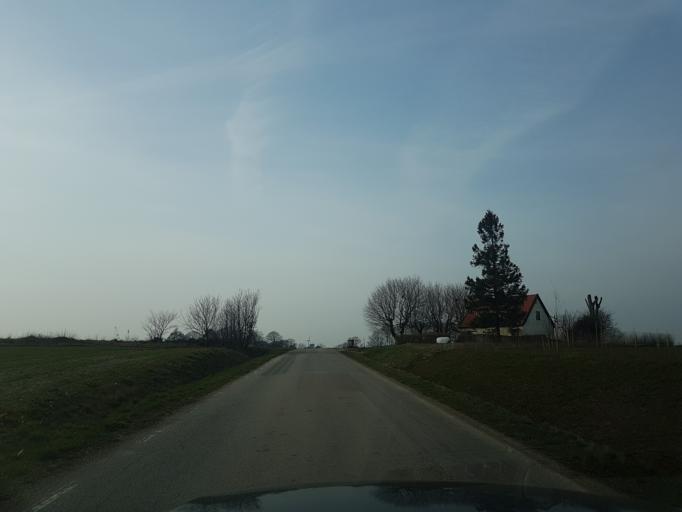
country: SE
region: Skane
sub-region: Ystads Kommun
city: Ystad
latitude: 55.4692
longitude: 13.8057
